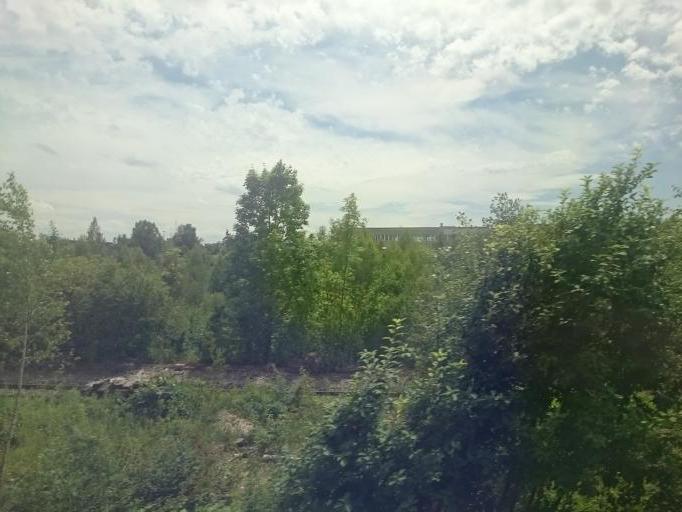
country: DE
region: Bavaria
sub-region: Upper Bavaria
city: Bogenhausen
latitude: 48.1345
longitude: 11.6259
